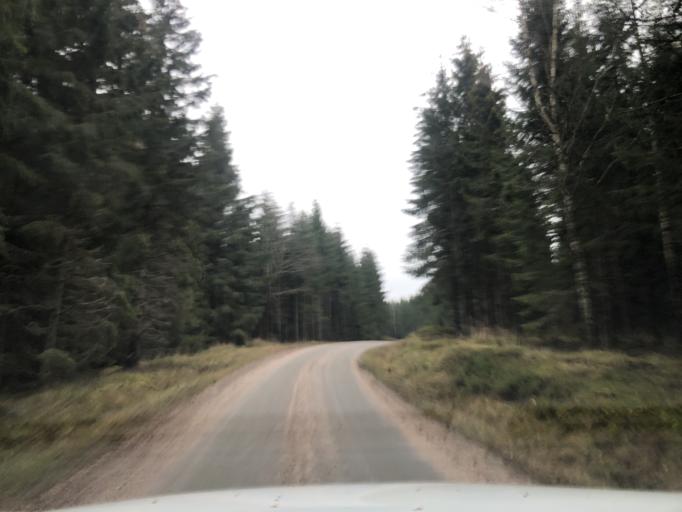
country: SE
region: Vaestra Goetaland
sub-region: Ulricehamns Kommun
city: Ulricehamn
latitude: 57.8703
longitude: 13.5577
